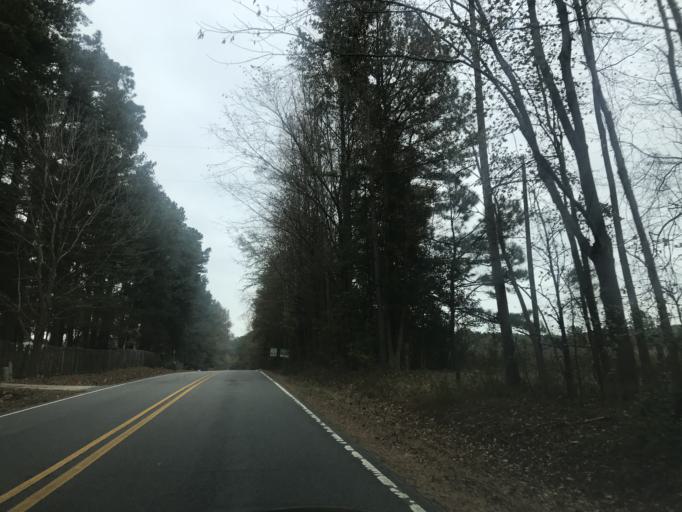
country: US
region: North Carolina
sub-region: Franklin County
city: Youngsville
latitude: 36.0035
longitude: -78.4928
